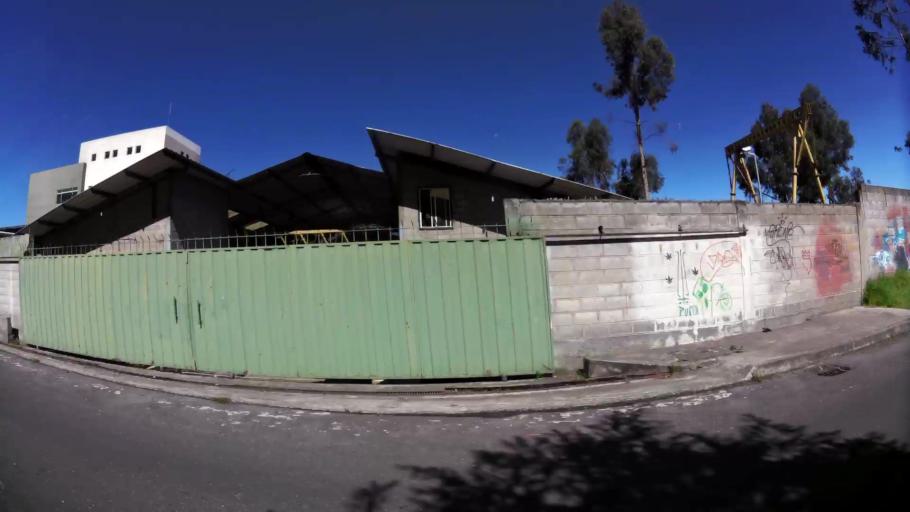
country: EC
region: Pichincha
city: Quito
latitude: -0.1225
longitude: -78.4781
